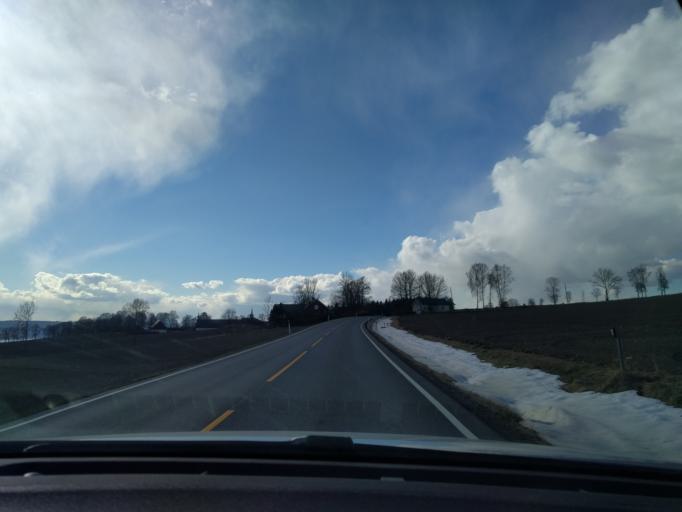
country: NO
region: Oppland
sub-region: Ostre Toten
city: Skreia
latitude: 60.7651
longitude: 10.9151
